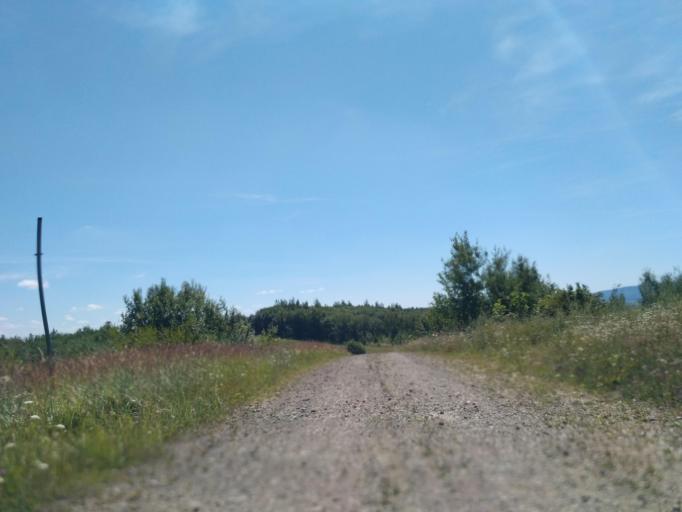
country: PL
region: Subcarpathian Voivodeship
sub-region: Powiat sanocki
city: Bukowsko
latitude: 49.5050
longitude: 22.0577
